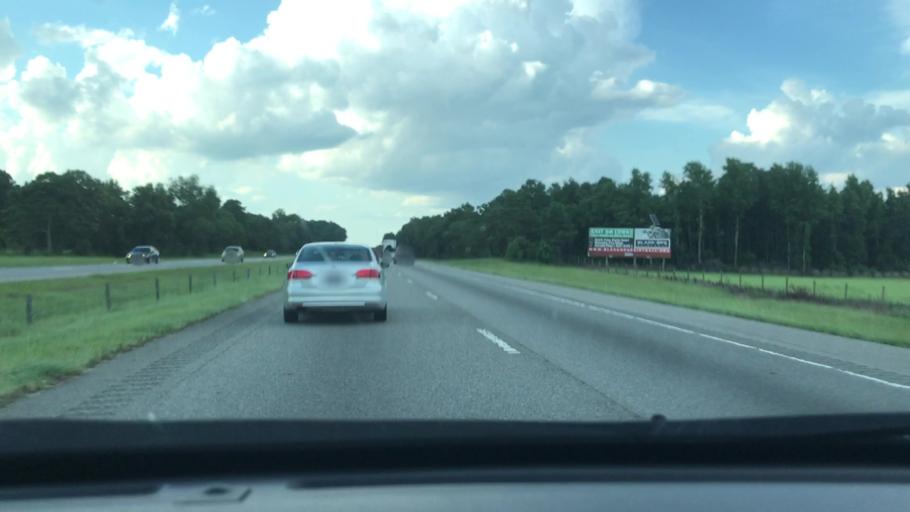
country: US
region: North Carolina
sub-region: Robeson County
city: Saint Pauls
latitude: 34.8681
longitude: -78.9639
